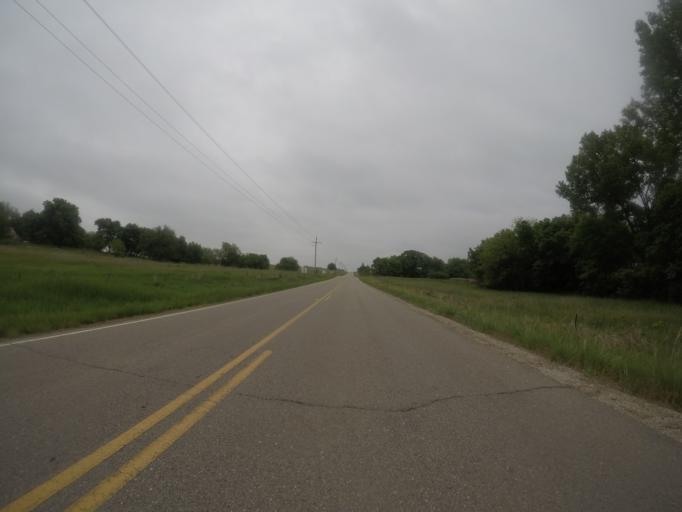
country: US
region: Kansas
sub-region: Pottawatomie County
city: Westmoreland
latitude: 39.5222
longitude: -96.2642
